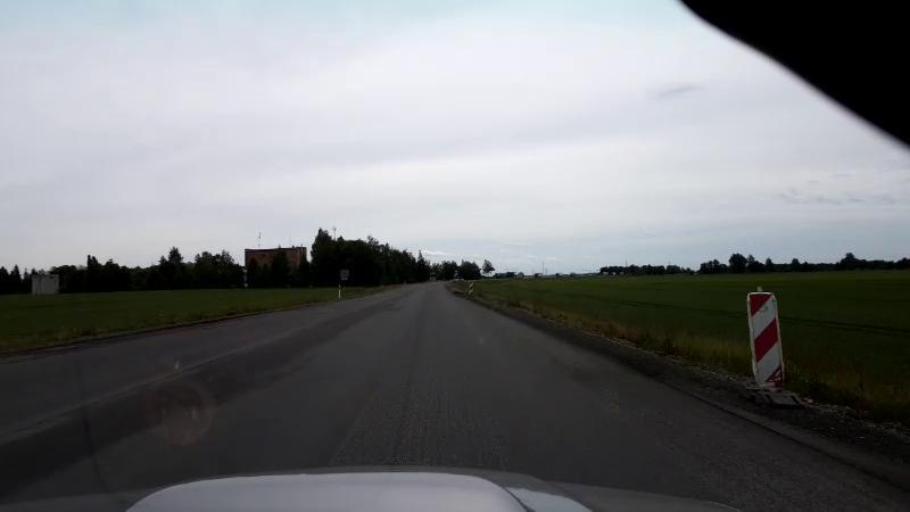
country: LV
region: Bauskas Rajons
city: Bauska
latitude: 56.3109
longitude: 24.3361
